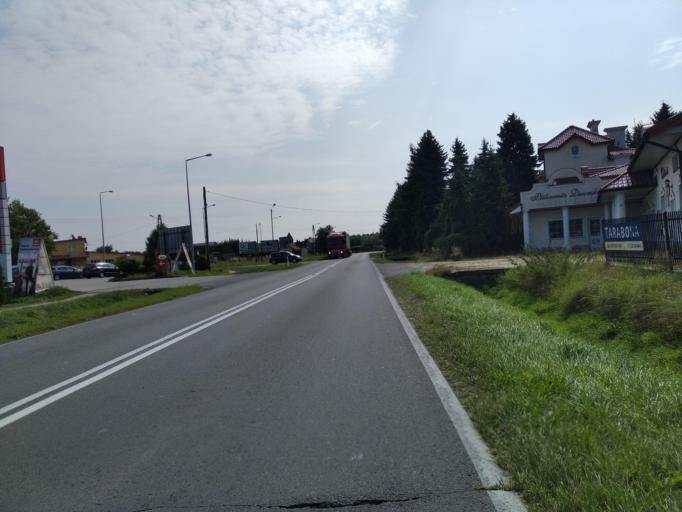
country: PL
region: Subcarpathian Voivodeship
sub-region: Powiat ropczycko-sedziszowski
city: Ostrow
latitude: 50.0738
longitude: 21.5847
